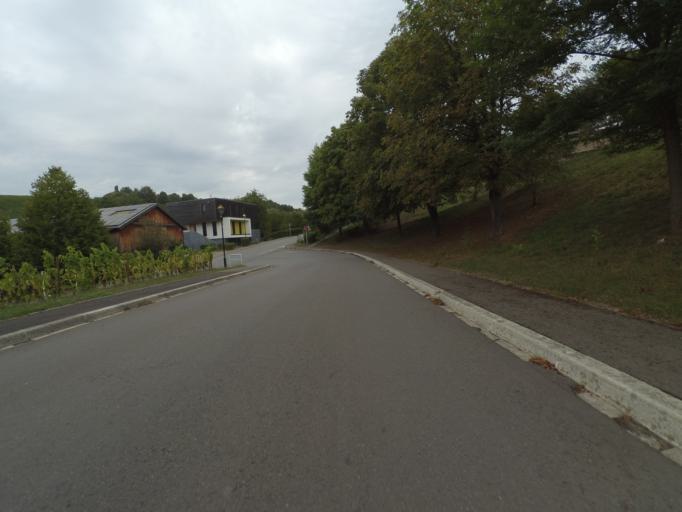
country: LU
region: Grevenmacher
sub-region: Canton de Grevenmacher
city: Wormeldange
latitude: 49.6050
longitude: 6.3891
